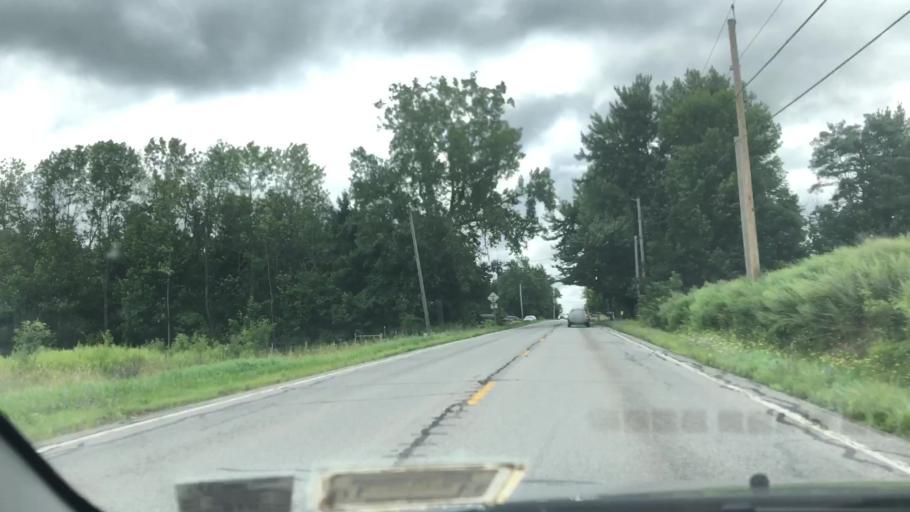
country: US
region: New York
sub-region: Wayne County
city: Macedon
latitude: 43.1132
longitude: -77.2932
